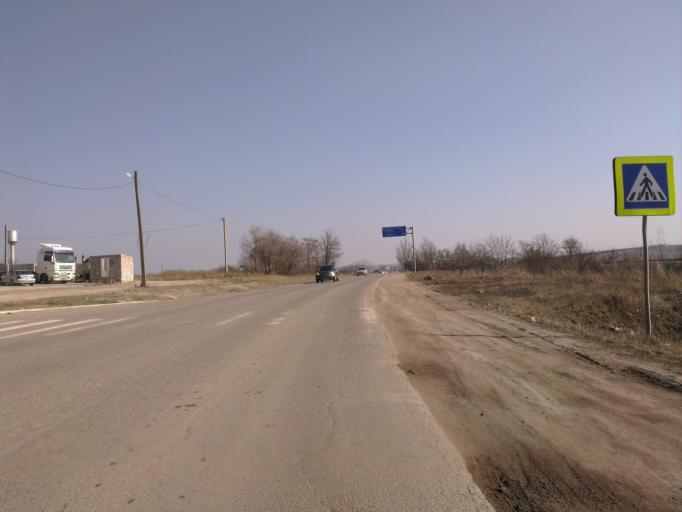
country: MD
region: Chisinau
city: Ciorescu
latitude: 47.1192
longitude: 28.8745
